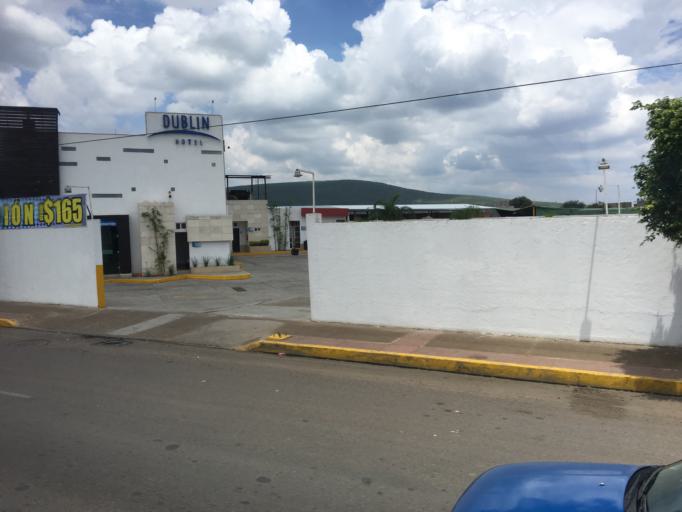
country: MX
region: Guanajuato
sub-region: Irapuato
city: Ex-Hacienda del Copal
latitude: 20.7121
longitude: -101.3511
